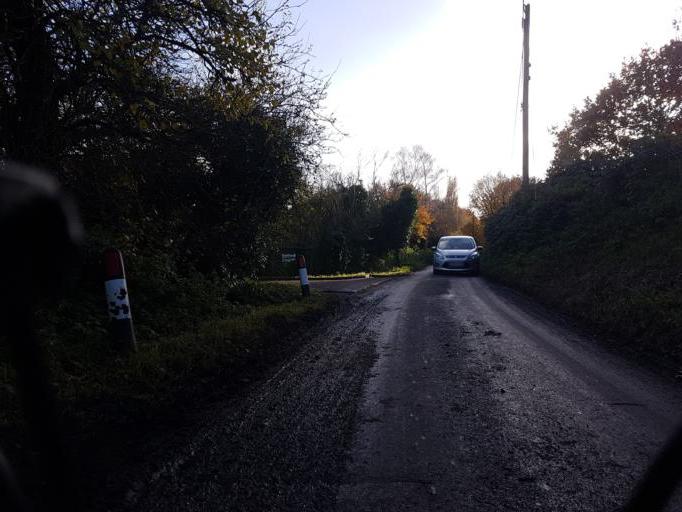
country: GB
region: England
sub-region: Kent
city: Newington
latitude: 51.3583
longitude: 0.6690
